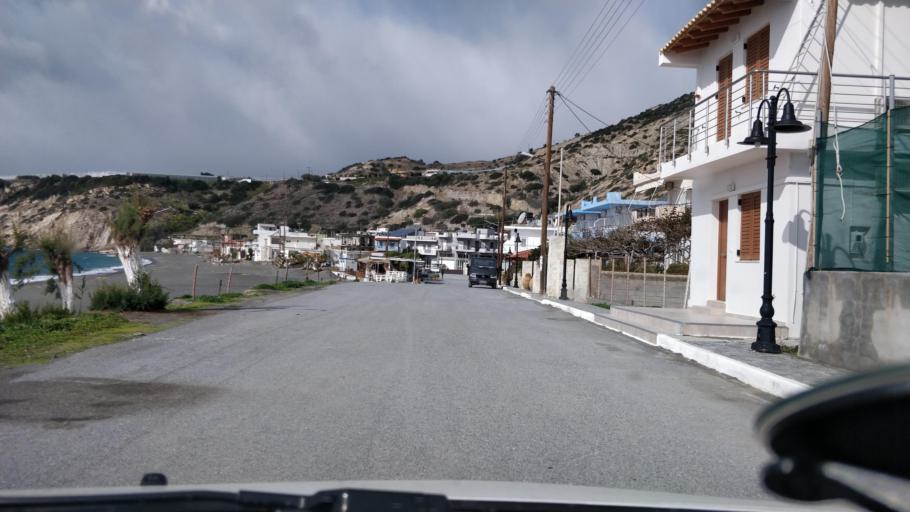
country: GR
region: Crete
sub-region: Nomos Lasithiou
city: Gra Liyia
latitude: 34.9842
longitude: 25.4991
